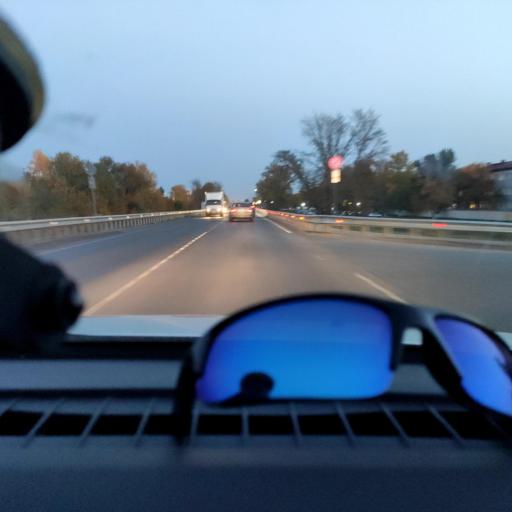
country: RU
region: Samara
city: Samara
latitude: 53.1187
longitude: 50.1214
